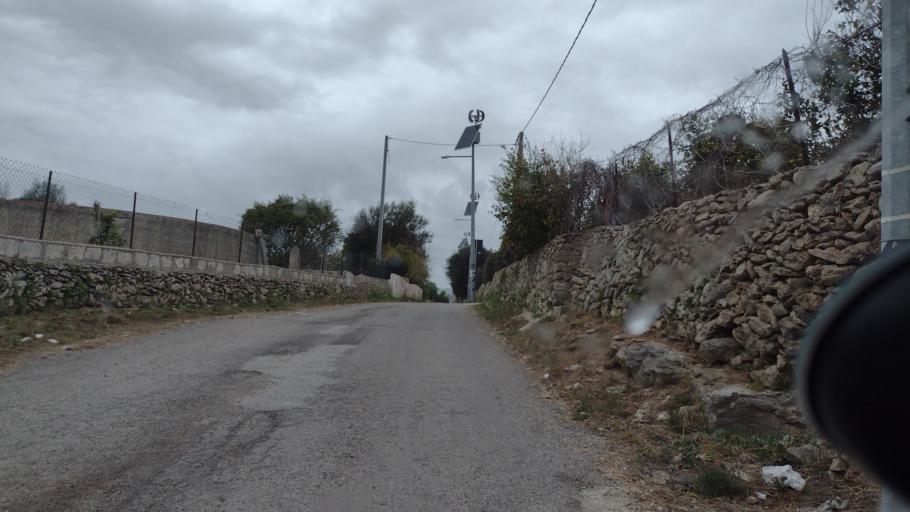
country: IT
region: Sicily
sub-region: Provincia di Siracusa
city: Avola
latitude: 36.8845
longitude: 15.1254
